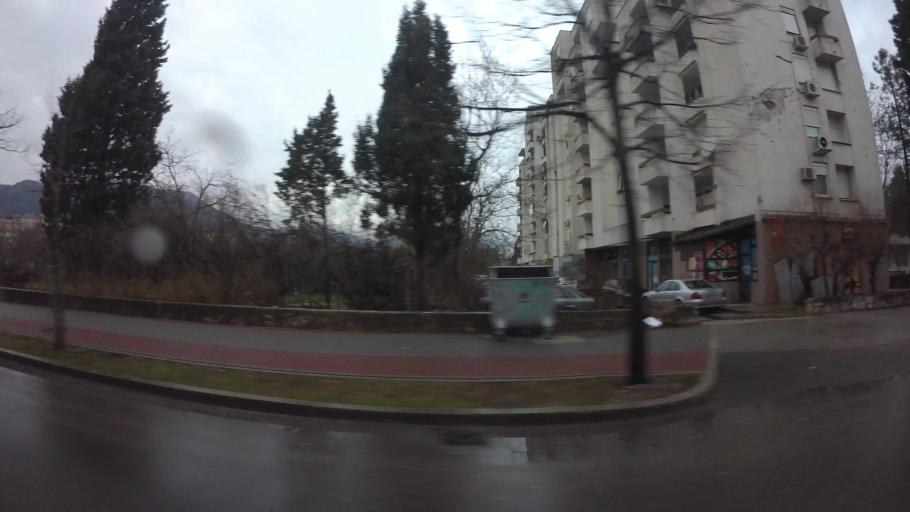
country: BA
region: Federation of Bosnia and Herzegovina
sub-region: Hercegovacko-Bosanski Kanton
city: Mostar
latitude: 43.3439
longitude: 17.8037
